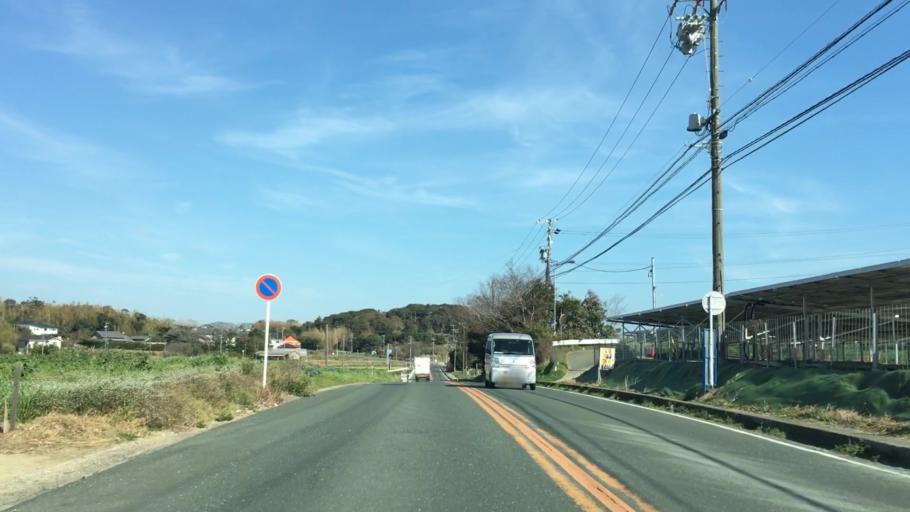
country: JP
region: Aichi
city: Toyohashi
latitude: 34.6777
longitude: 137.4322
